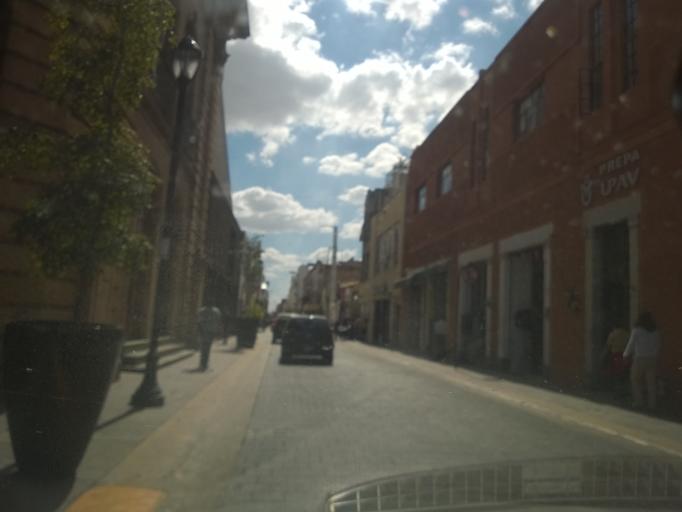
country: MX
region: Guanajuato
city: Leon
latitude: 21.1229
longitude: -101.6802
